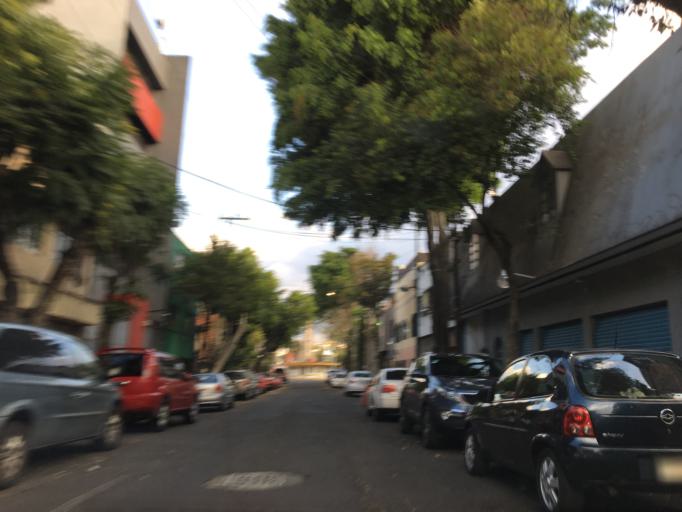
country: MX
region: Mexico City
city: Cuauhtemoc
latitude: 19.4632
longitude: -99.1461
